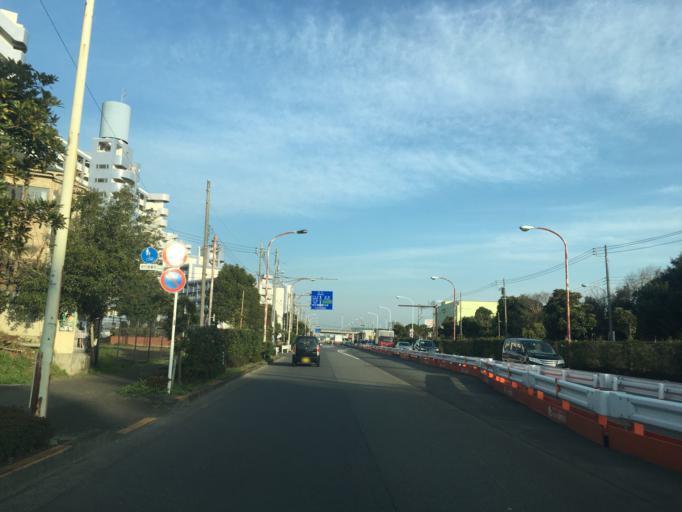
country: JP
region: Tokyo
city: Hino
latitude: 35.6728
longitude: 139.4327
